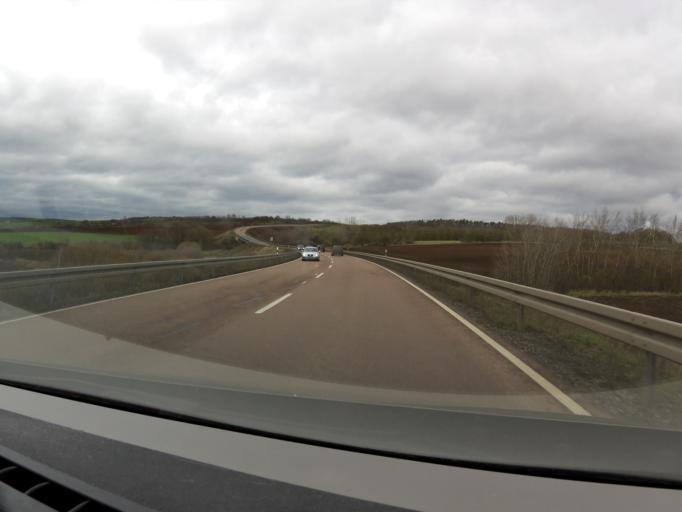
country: DE
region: Saxony-Anhalt
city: Riestedt
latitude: 51.5014
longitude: 11.3800
